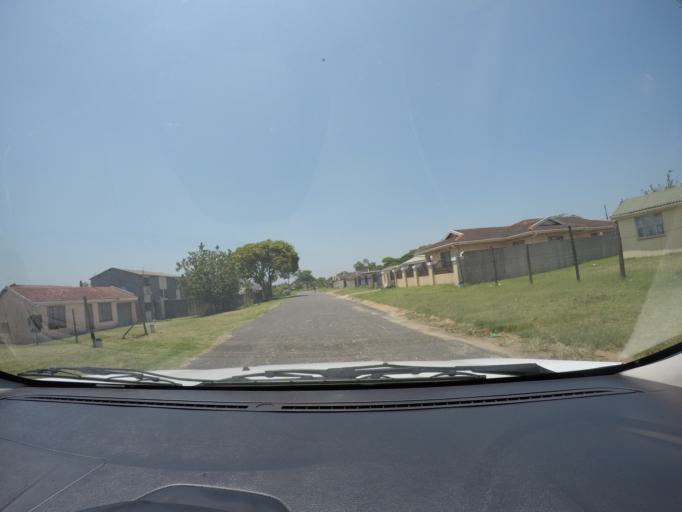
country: ZA
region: KwaZulu-Natal
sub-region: uThungulu District Municipality
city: eSikhawini
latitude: -28.8822
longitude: 31.8910
